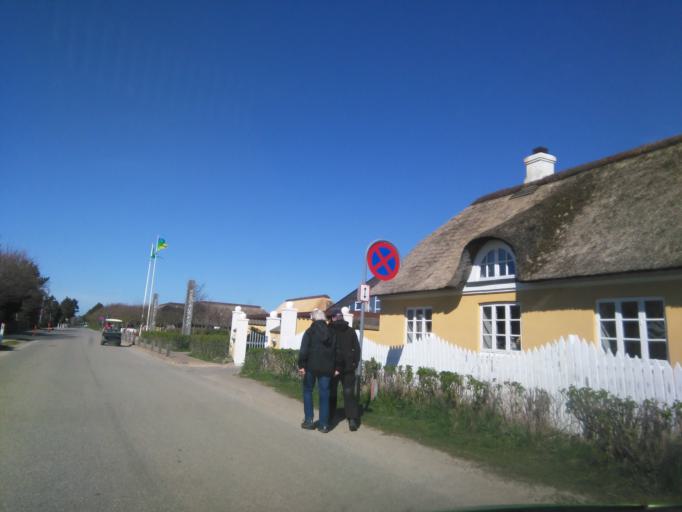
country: DK
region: South Denmark
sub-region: Varde Kommune
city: Oksbol
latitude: 55.5454
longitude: 8.1338
